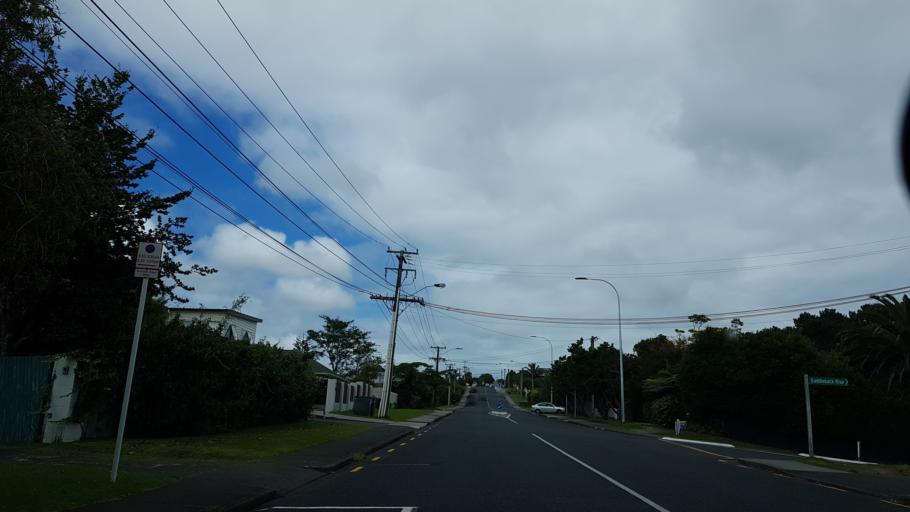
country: NZ
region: Auckland
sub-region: Auckland
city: Rothesay Bay
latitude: -36.7347
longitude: 174.7422
